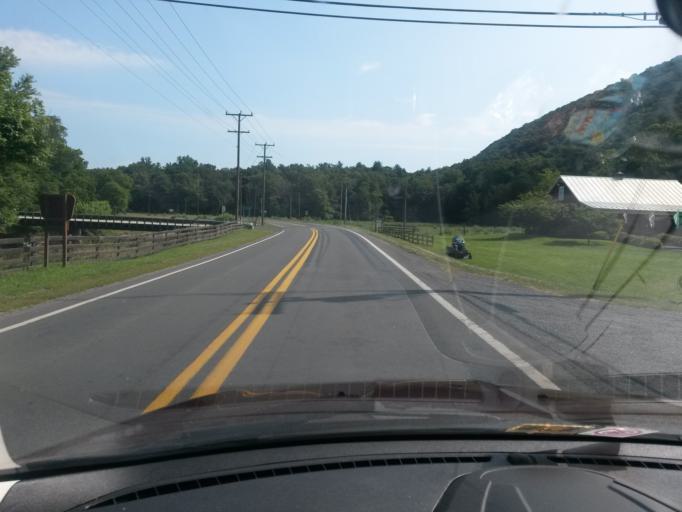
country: US
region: Virginia
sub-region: Shenandoah County
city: Basye
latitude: 38.9532
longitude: -78.8044
